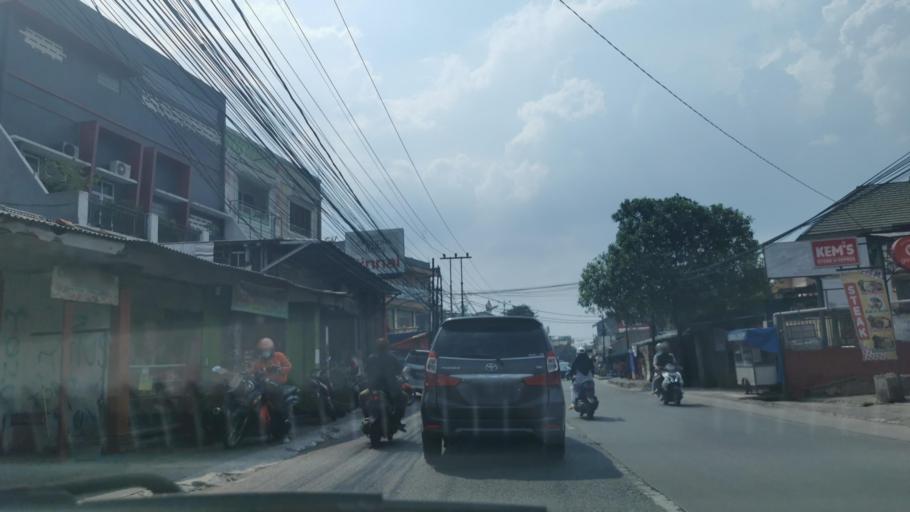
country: ID
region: West Java
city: Depok
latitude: -6.4019
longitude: 106.8371
